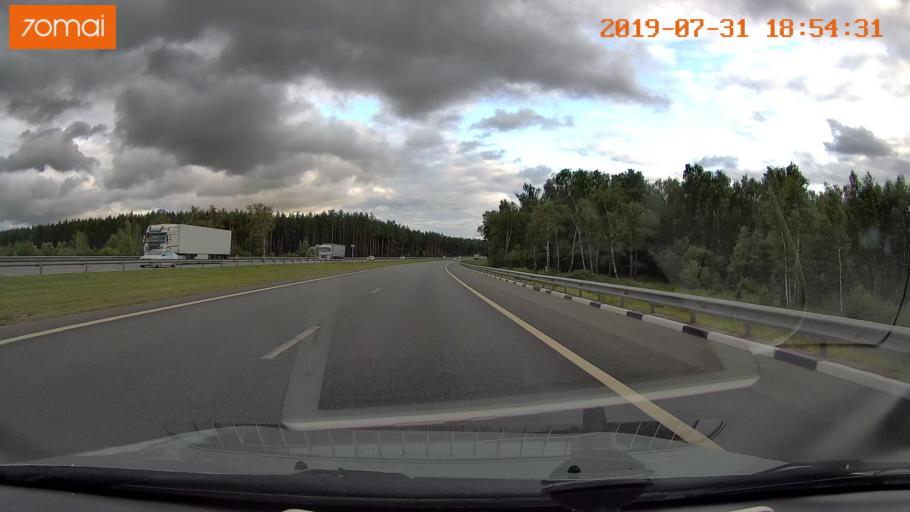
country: RU
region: Moskovskaya
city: Raduzhnyy
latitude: 55.1887
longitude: 38.6685
